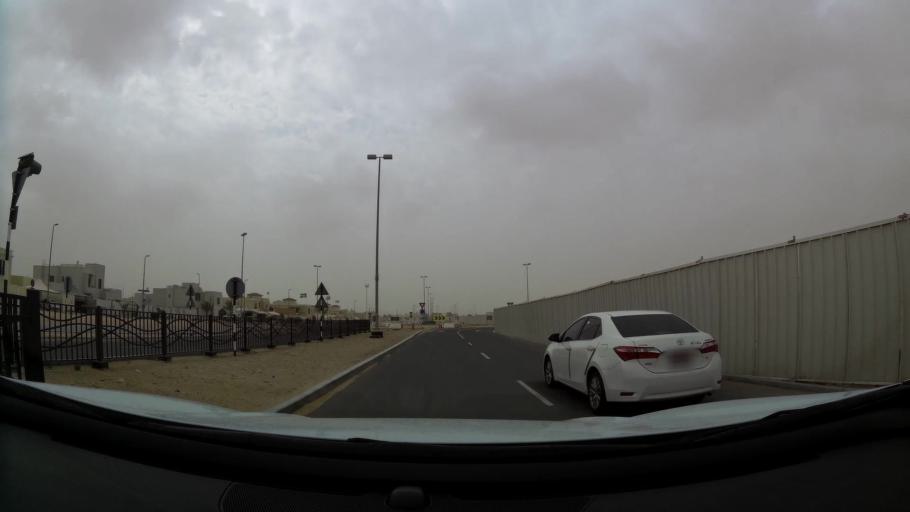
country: AE
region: Abu Dhabi
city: Abu Dhabi
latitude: 24.4333
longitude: 54.7266
